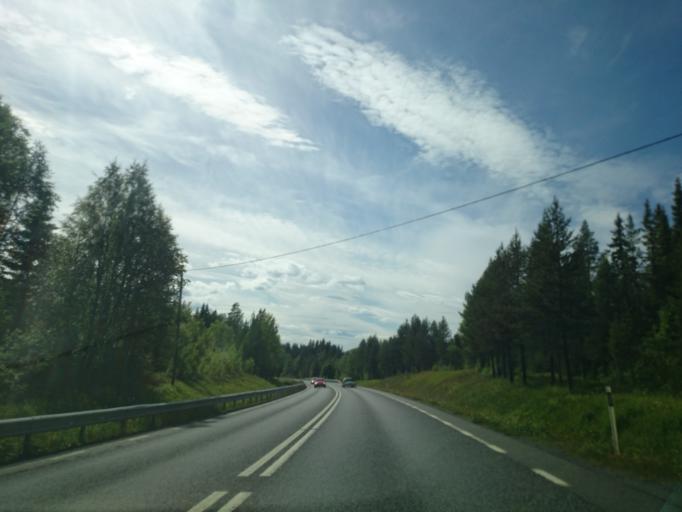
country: SE
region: Jaemtland
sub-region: Krokoms Kommun
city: Valla
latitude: 63.3376
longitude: 13.9889
